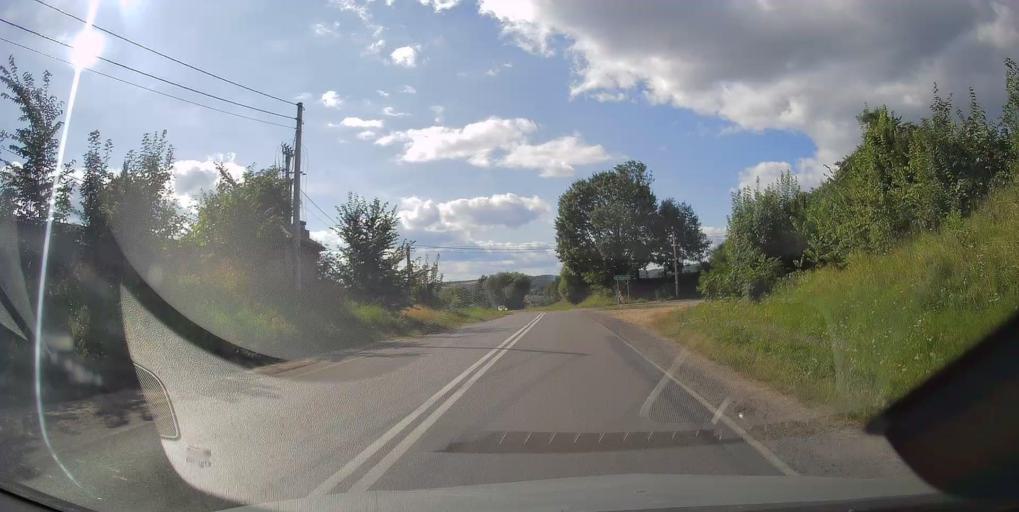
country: PL
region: Swietokrzyskie
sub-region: Powiat kielecki
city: Bodzentyn
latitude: 50.9714
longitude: 20.8801
